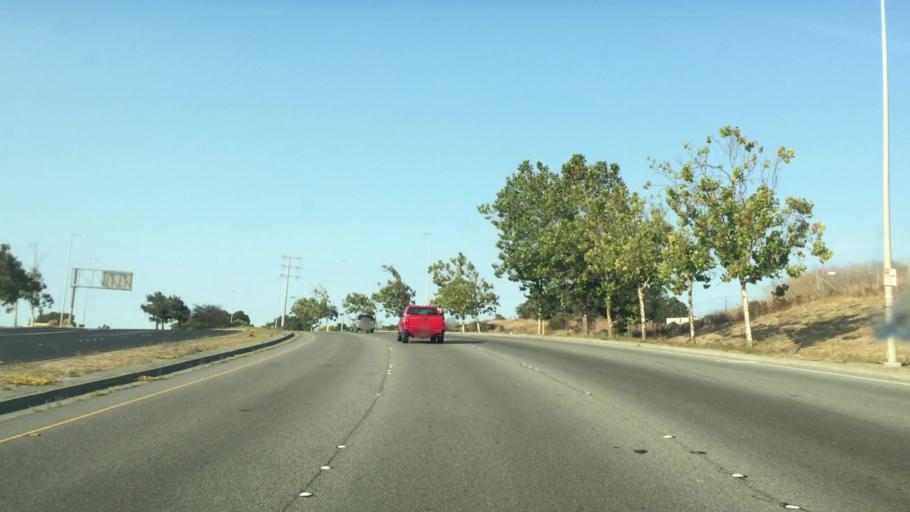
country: US
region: California
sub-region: Contra Costa County
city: Montalvin
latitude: 37.9825
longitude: -122.3435
